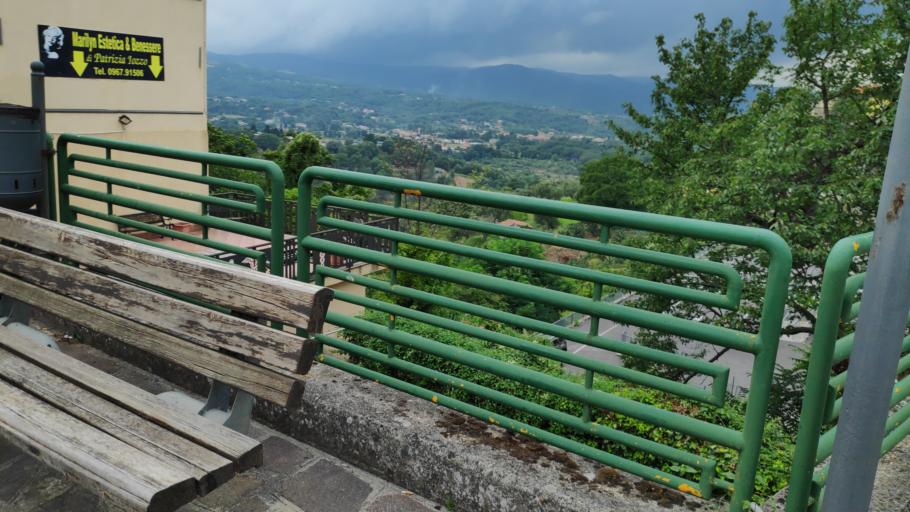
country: IT
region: Calabria
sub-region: Provincia di Catanzaro
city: Chiaravalle Centrale
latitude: 38.6819
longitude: 16.4139
